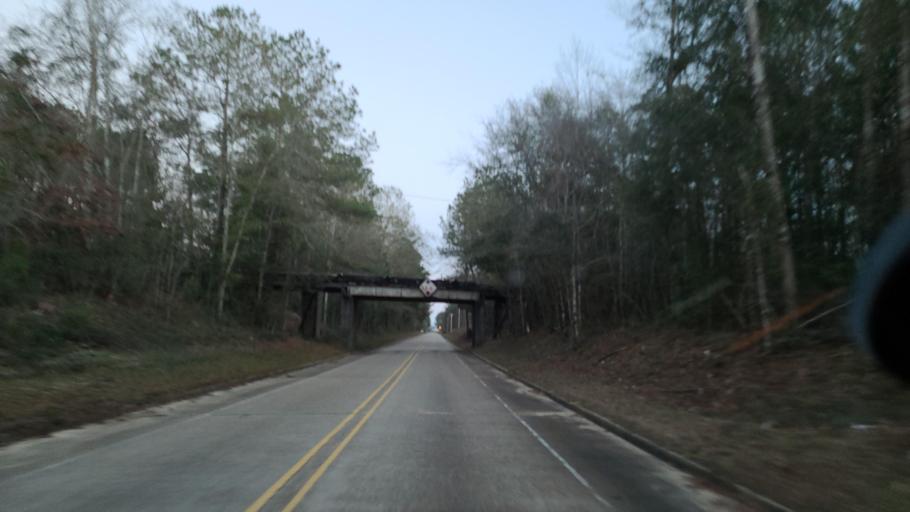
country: US
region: Mississippi
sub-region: Forrest County
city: Hattiesburg
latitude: 31.2110
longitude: -89.2532
